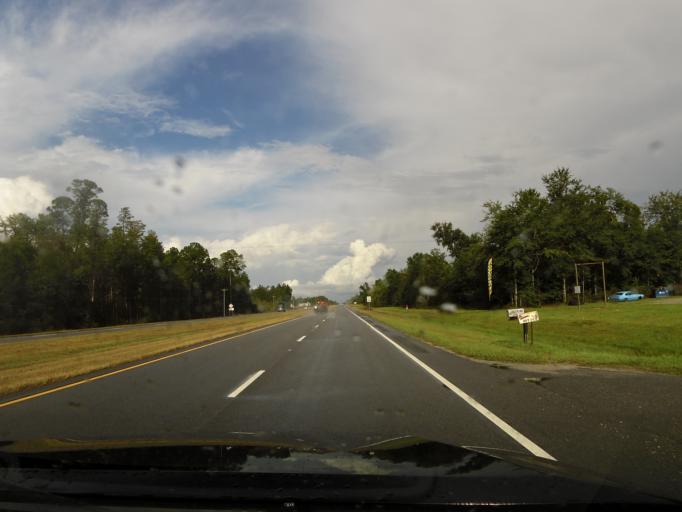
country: US
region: Georgia
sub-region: Liberty County
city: Walthourville
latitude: 31.7537
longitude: -81.6700
